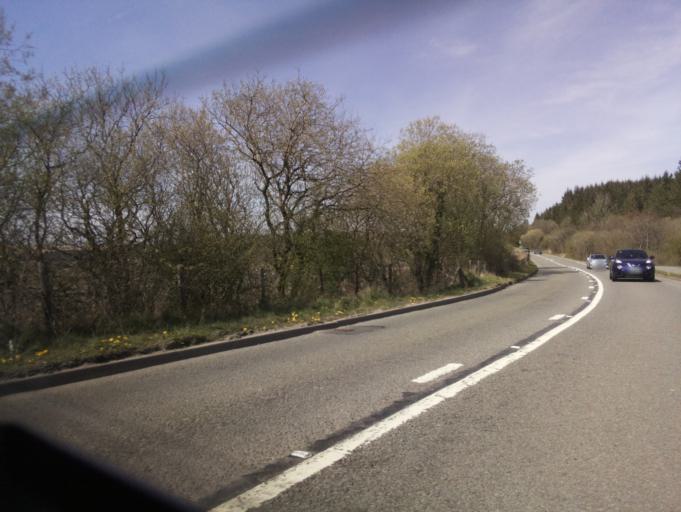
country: GB
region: Wales
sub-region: Rhondda Cynon Taf
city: Aberdare
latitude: 51.7475
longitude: -3.4419
